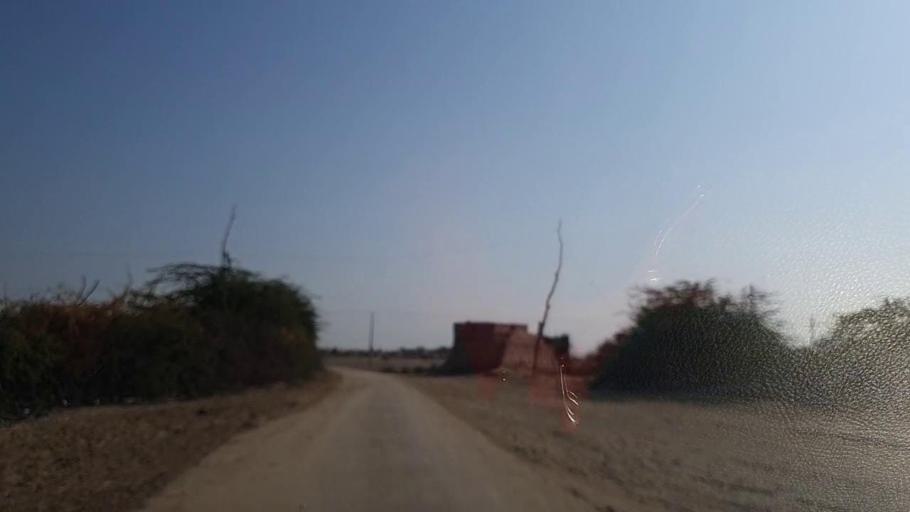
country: PK
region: Sindh
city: Tando Mittha Khan
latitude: 26.0289
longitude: 69.1153
